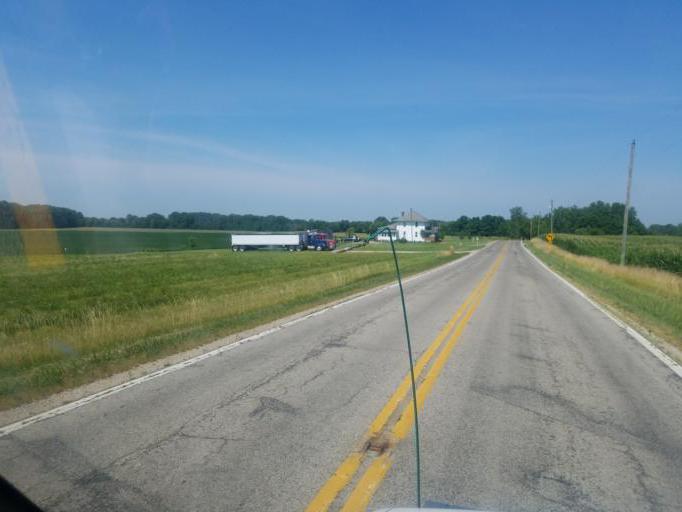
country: US
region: Ohio
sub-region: Champaign County
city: North Lewisburg
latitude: 40.2298
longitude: -83.5103
